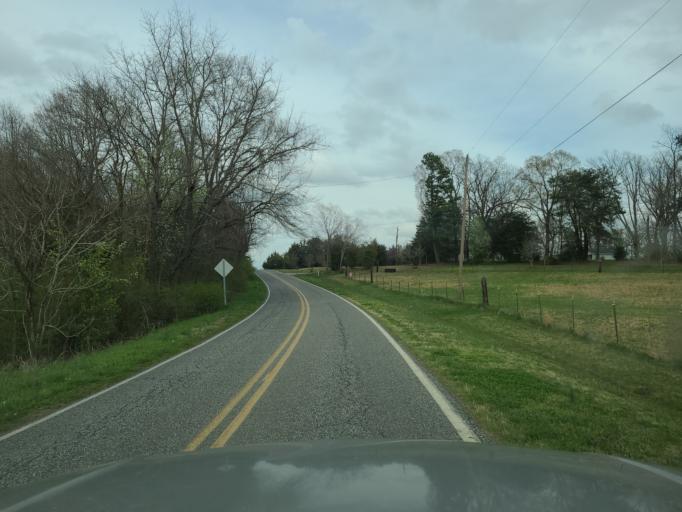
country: US
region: North Carolina
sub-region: Cleveland County
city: Boiling Springs
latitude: 35.2377
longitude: -81.7218
